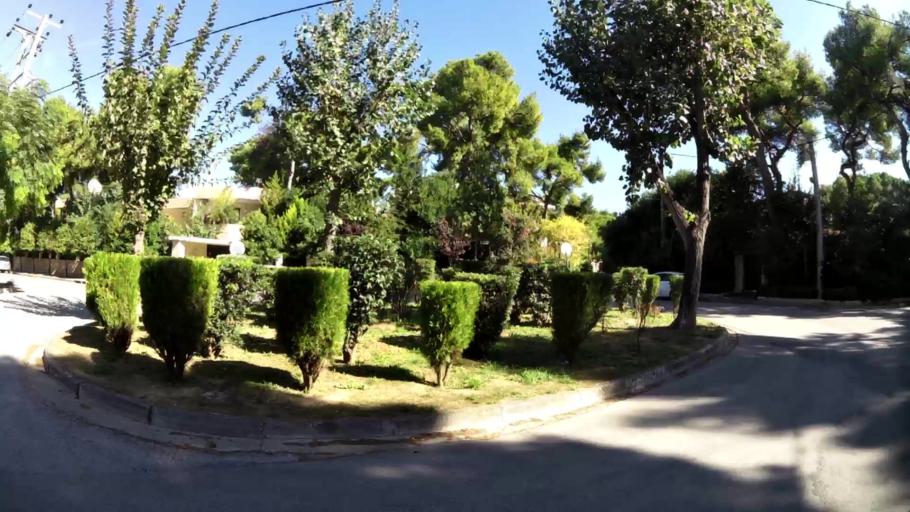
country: GR
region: Attica
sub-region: Nomarchia Athinas
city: Nea Erythraia
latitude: 38.0943
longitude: 23.8009
